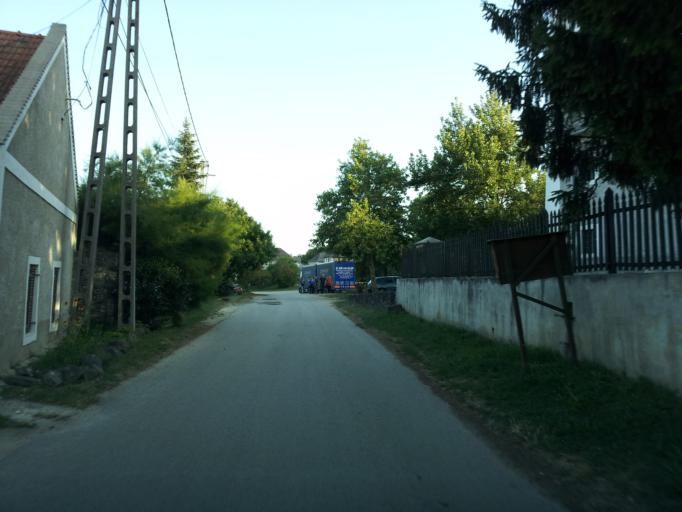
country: HU
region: Veszprem
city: Ajka
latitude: 46.9819
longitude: 17.5679
